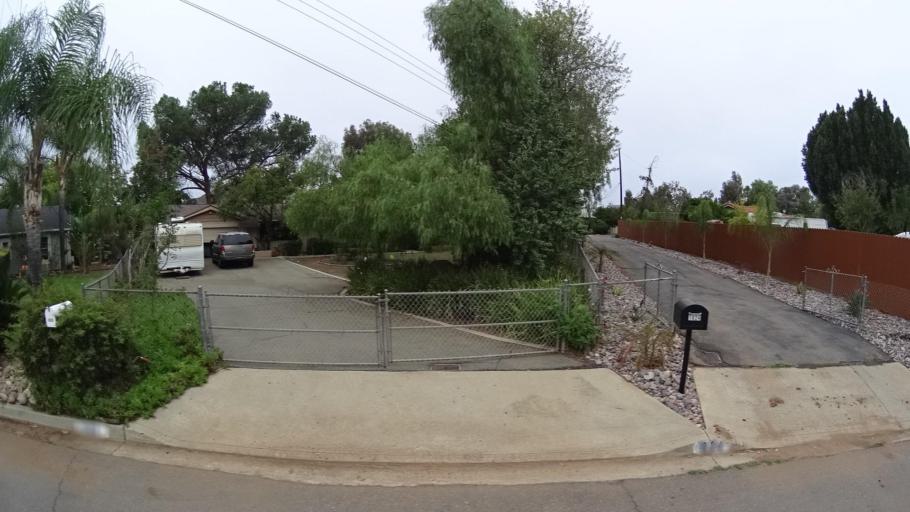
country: US
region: California
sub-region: San Diego County
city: Rancho San Diego
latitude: 32.7577
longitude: -116.9185
